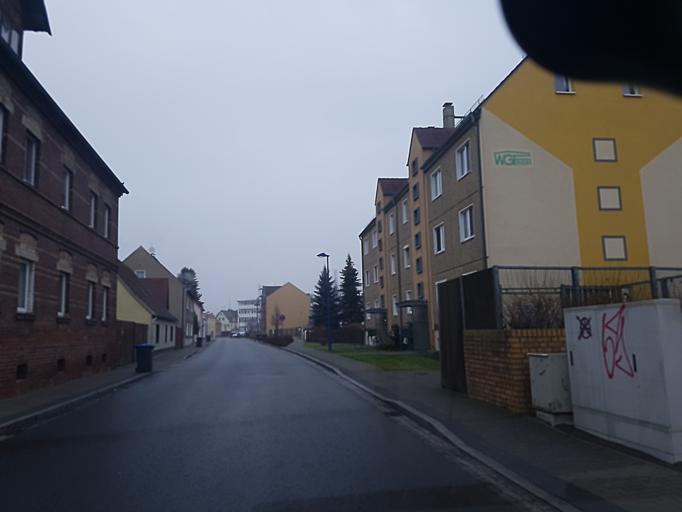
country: DE
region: Brandenburg
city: Finsterwalde
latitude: 51.6247
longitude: 13.7048
